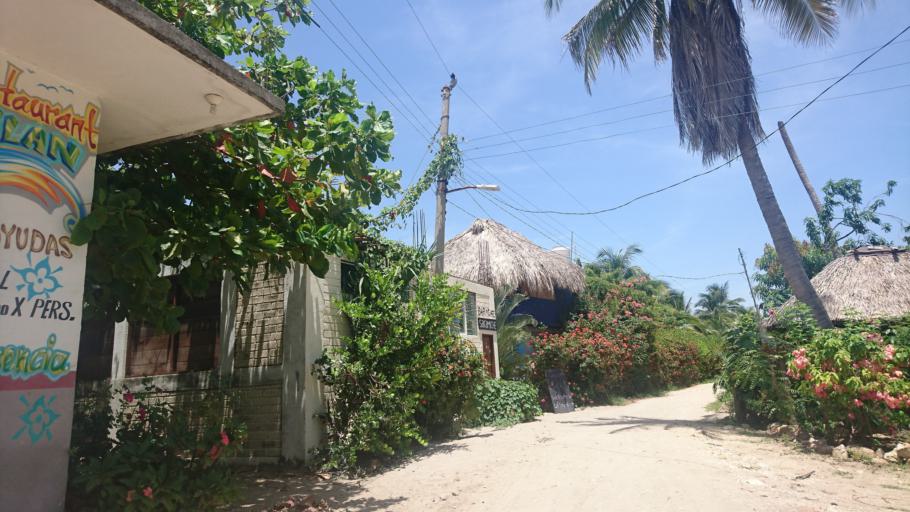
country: MX
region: Oaxaca
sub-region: Villa de Tututepec de Melchor Ocampo
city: Santa Rosa de Lima
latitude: 15.9686
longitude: -97.6792
